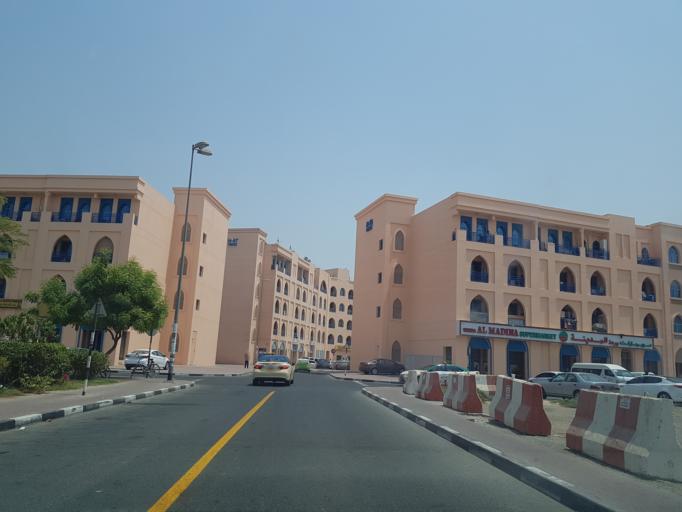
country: AE
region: Ash Shariqah
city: Sharjah
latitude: 25.1577
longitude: 55.4068
